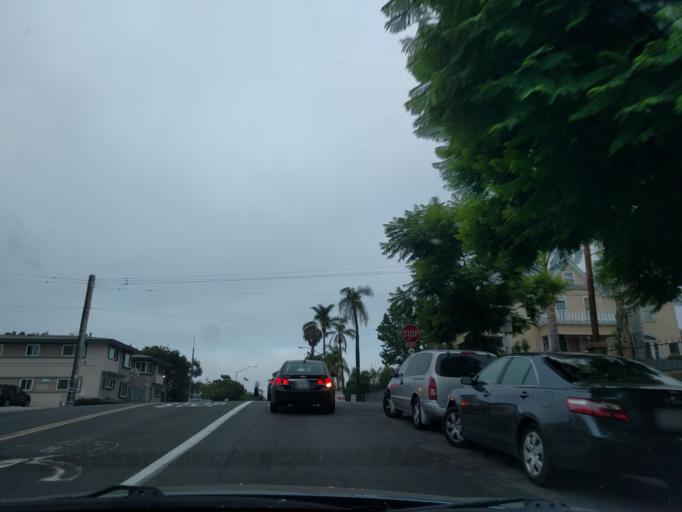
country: US
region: California
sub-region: San Diego County
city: San Diego
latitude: 32.7159
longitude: -117.1379
